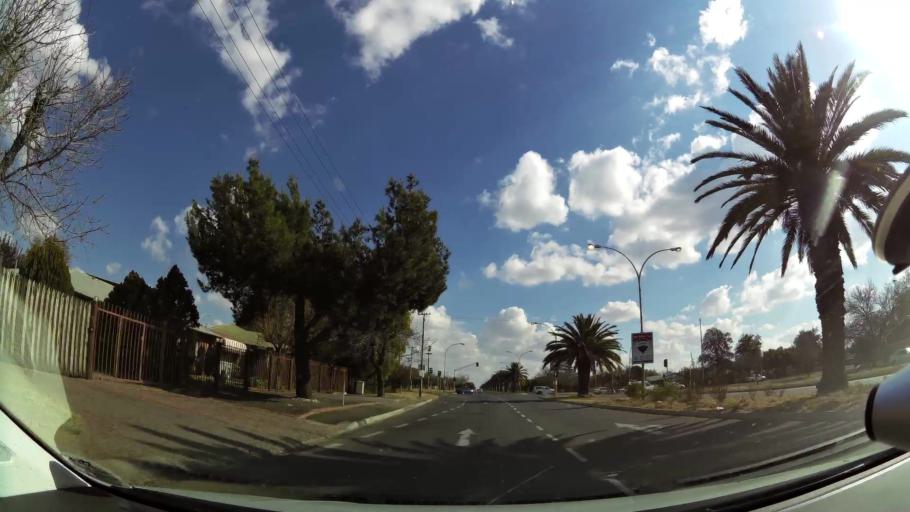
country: ZA
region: Orange Free State
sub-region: Mangaung Metropolitan Municipality
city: Bloemfontein
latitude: -29.1265
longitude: 26.1783
